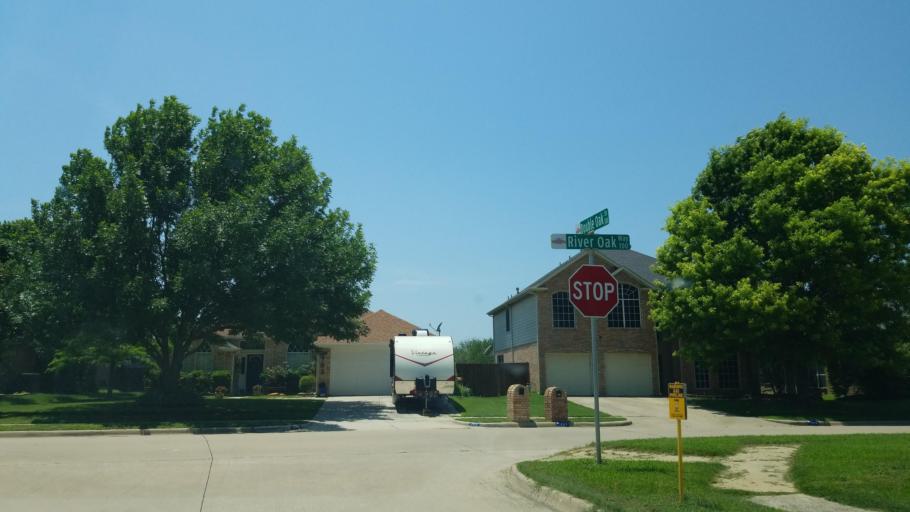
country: US
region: Texas
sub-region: Denton County
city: Hickory Creek
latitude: 33.1397
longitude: -97.0378
